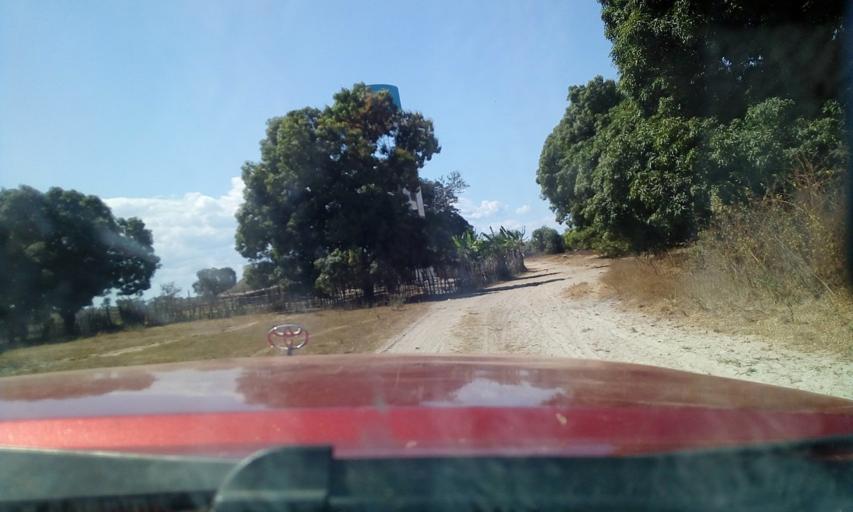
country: MG
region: Boeny
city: Sitampiky
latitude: -16.1249
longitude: 45.5109
